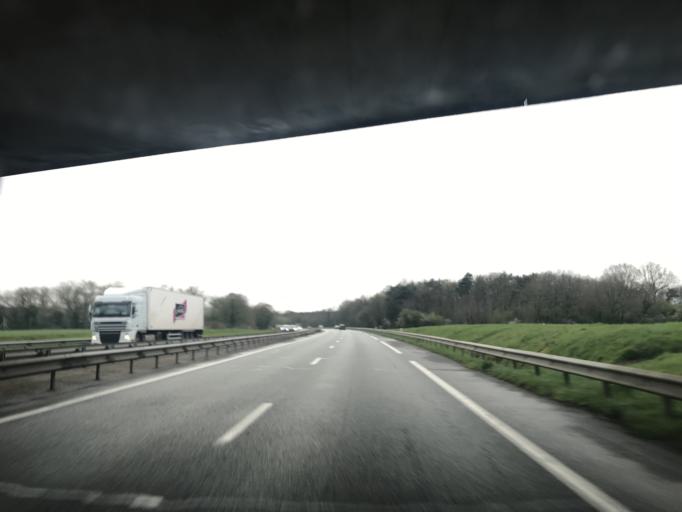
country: FR
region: Centre
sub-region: Departement du Loiret
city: Fay-aux-Loges
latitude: 47.9098
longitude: 2.1618
